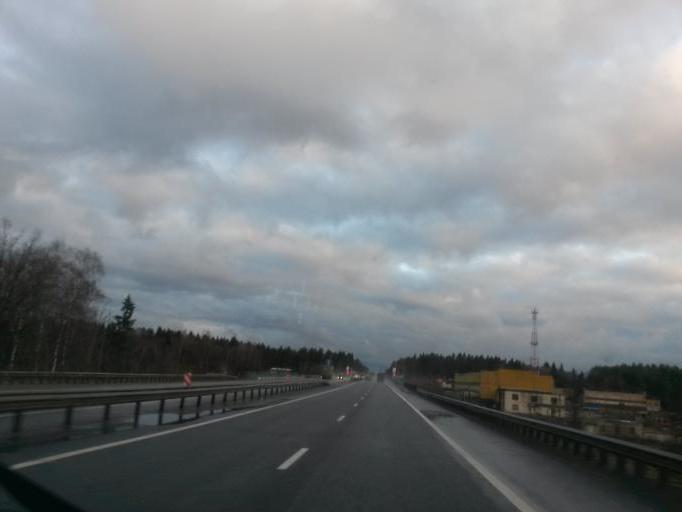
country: RU
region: Moskovskaya
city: Svatkovo
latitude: 56.3876
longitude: 38.3265
